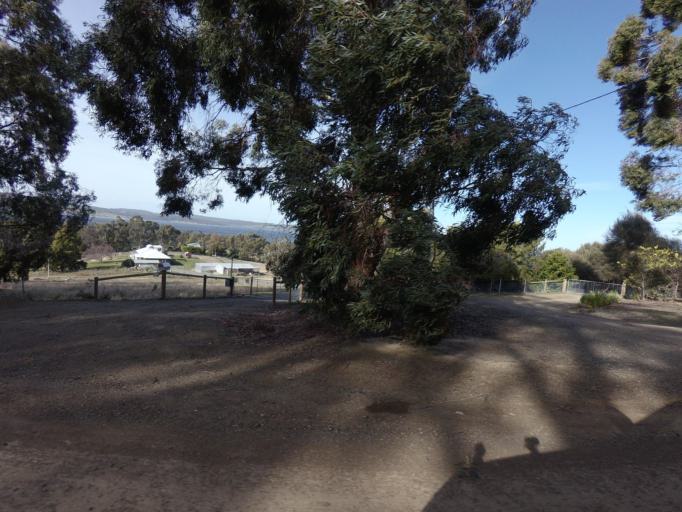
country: AU
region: Tasmania
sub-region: Kingborough
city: Kettering
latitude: -43.1198
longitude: 147.2641
